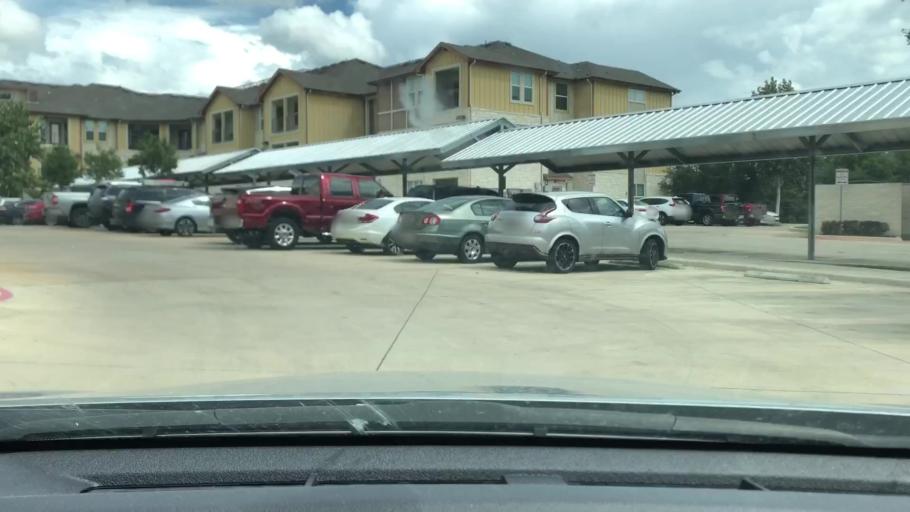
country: US
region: Texas
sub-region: Bexar County
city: Hollywood Park
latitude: 29.6145
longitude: -98.4804
